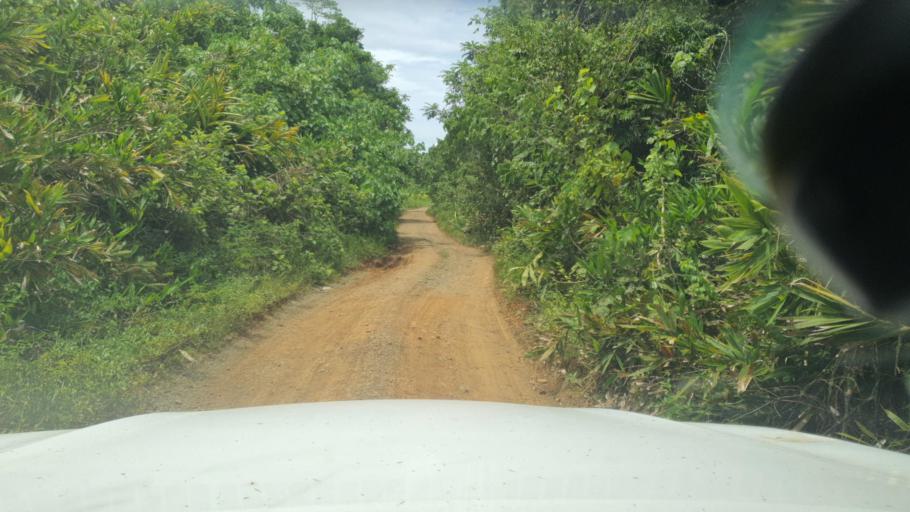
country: SB
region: Guadalcanal
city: Honiara
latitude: -9.4859
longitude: 160.3246
